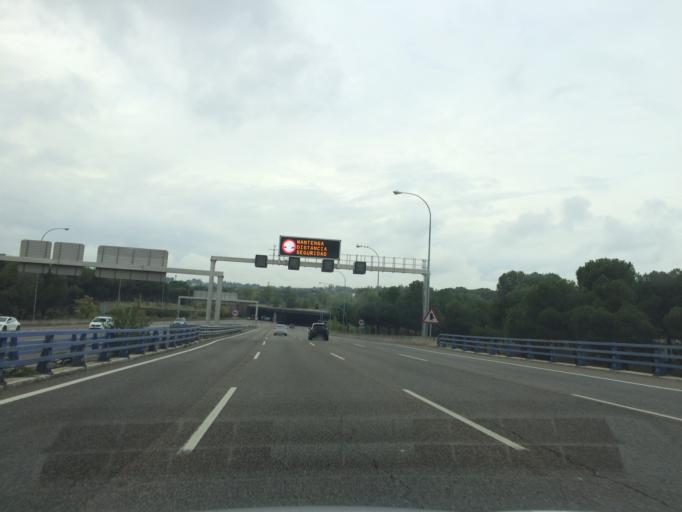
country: ES
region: Madrid
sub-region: Provincia de Madrid
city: Fuencarral-El Pardo
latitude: 40.4766
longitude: -3.7547
